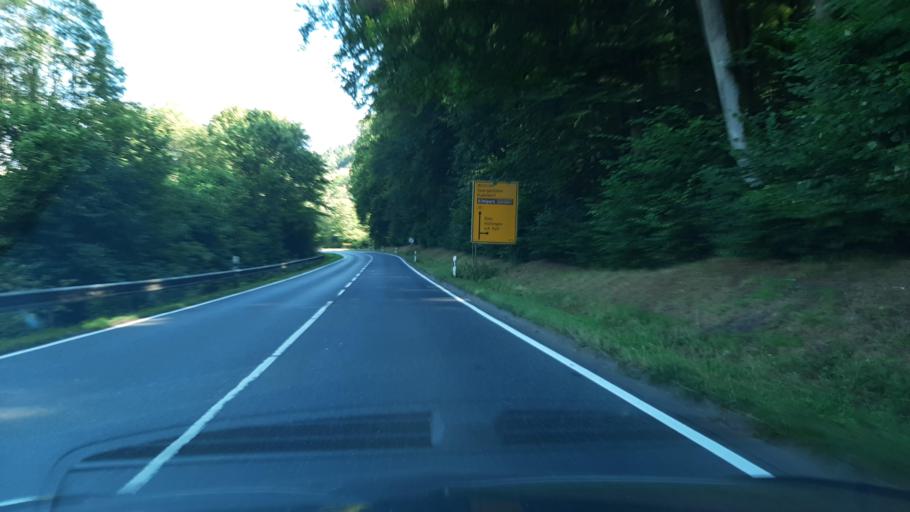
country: DE
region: Rheinland-Pfalz
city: Metterich
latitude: 49.9746
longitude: 6.5670
